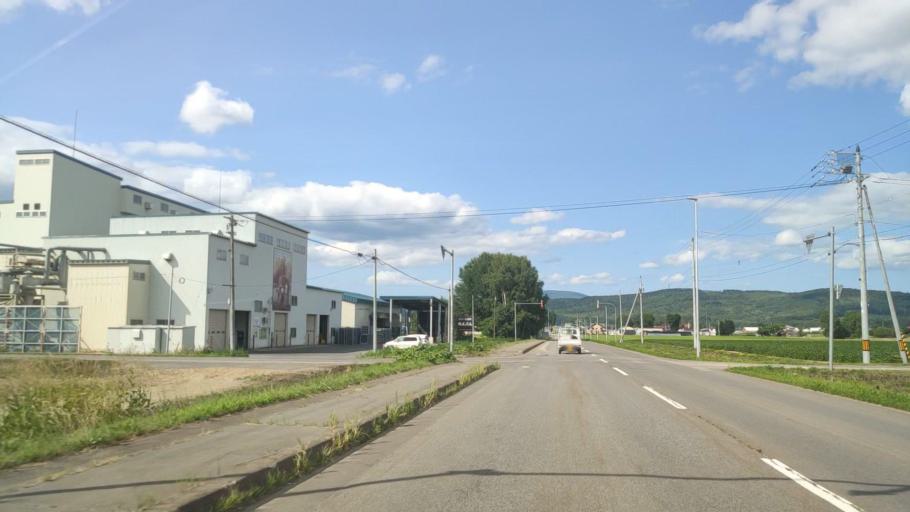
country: JP
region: Hokkaido
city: Nayoro
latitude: 44.4319
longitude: 142.4013
